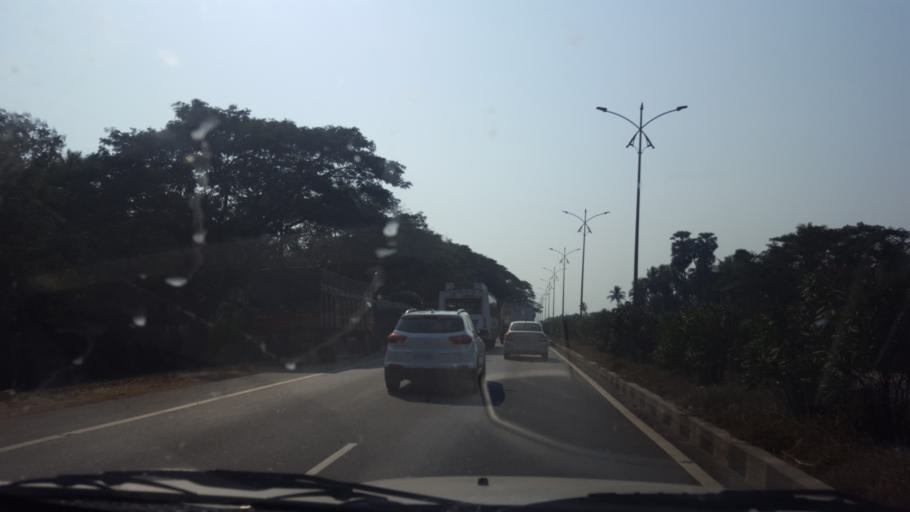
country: IN
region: Andhra Pradesh
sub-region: Vishakhapatnam
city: Anakapalle
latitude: 17.6768
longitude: 83.0212
